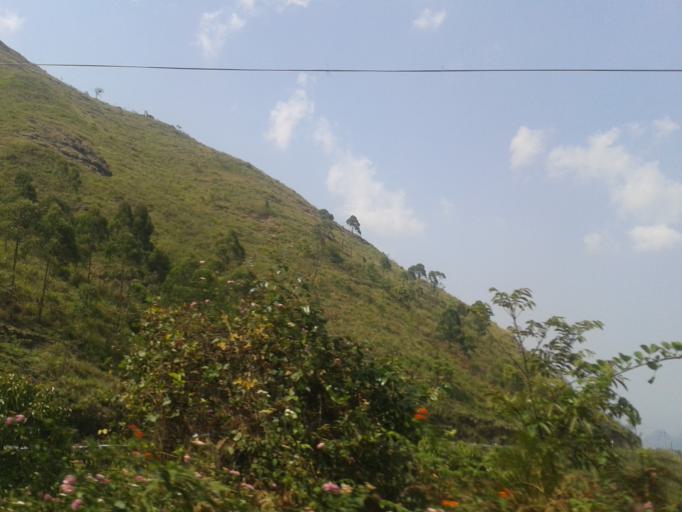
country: IN
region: Tamil Nadu
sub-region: Dindigul
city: Kodaikanal
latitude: 10.3255
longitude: 77.5637
